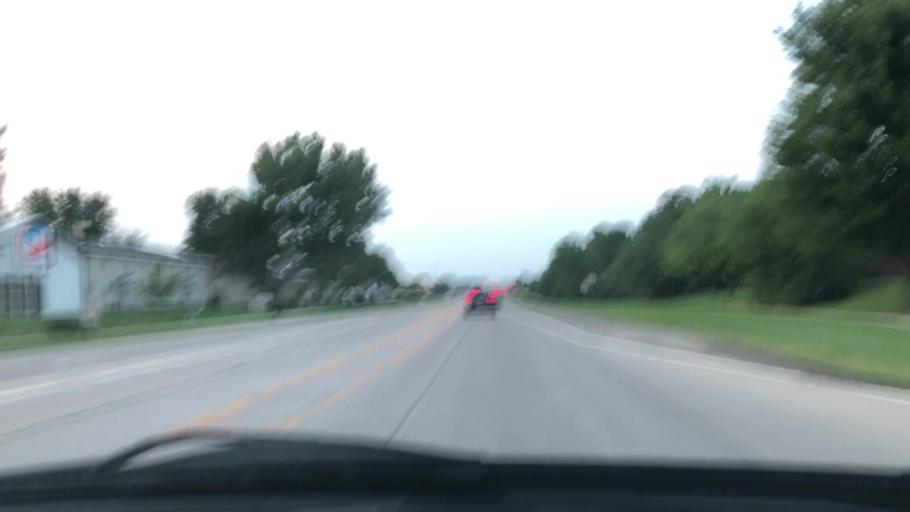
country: US
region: Iowa
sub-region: Johnson County
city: North Liberty
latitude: 41.7413
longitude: -91.6076
